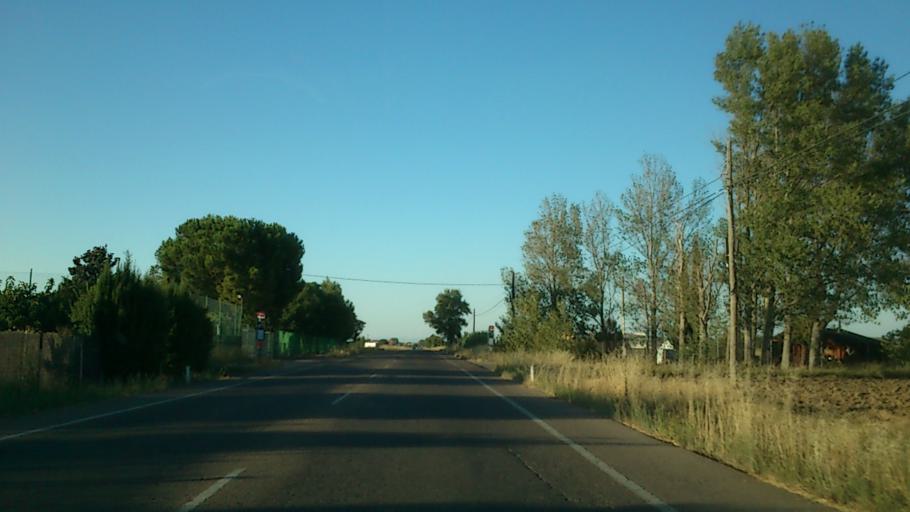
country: ES
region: Aragon
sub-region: Provincia de Zaragoza
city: Villanueva de Gallego
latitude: 41.7446
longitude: -0.8048
